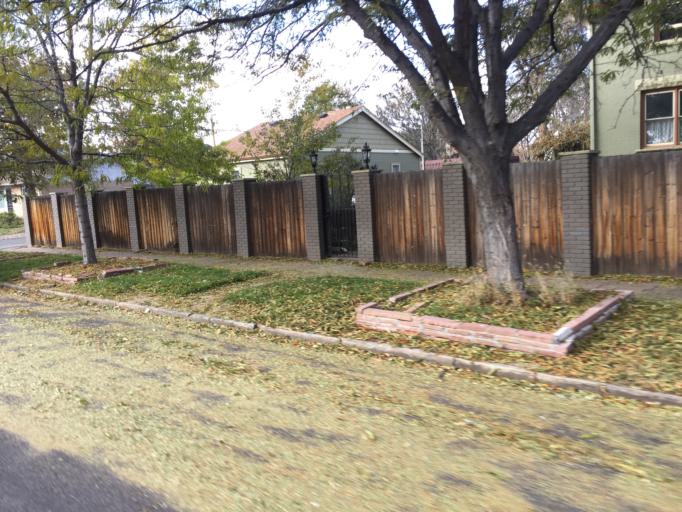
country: US
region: Colorado
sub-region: Denver County
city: Denver
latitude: 39.7570
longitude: -104.9711
